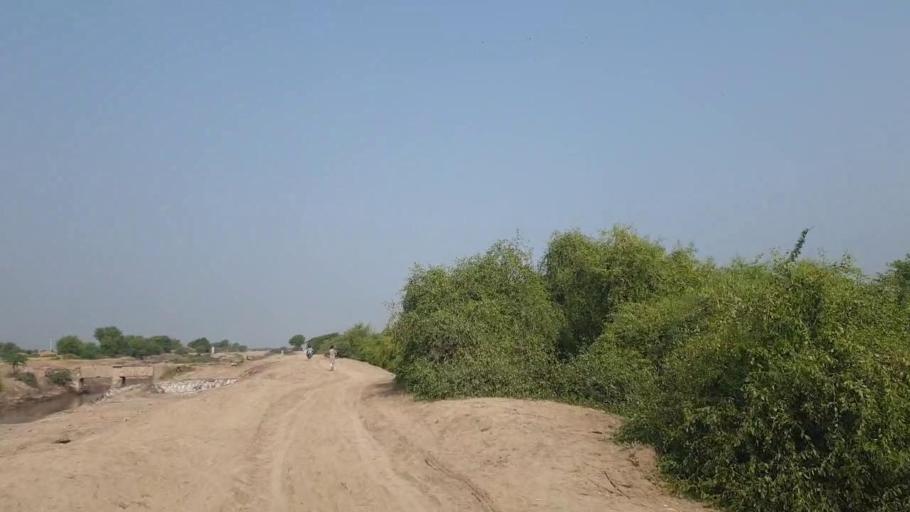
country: PK
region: Sindh
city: Badin
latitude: 24.7033
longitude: 68.7762
